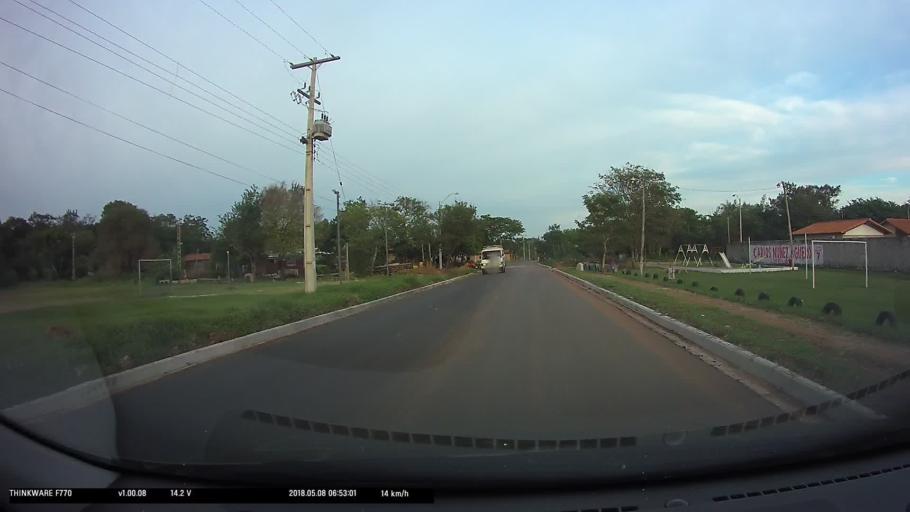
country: PY
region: Central
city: Limpio
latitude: -25.2348
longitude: -57.4685
